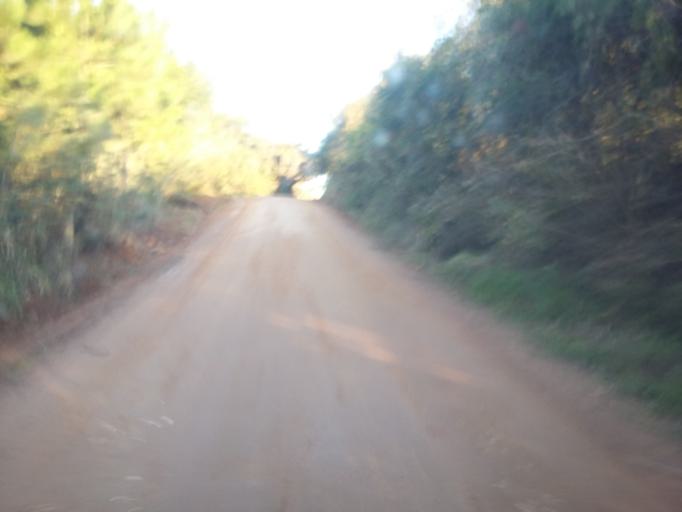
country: BR
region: Rio Grande do Sul
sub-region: Camaqua
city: Camaqua
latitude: -30.7347
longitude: -51.7755
